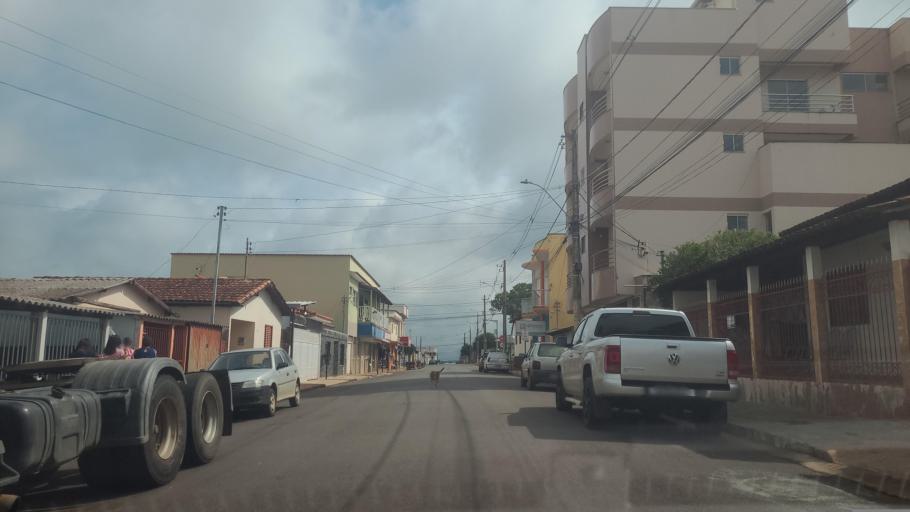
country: BR
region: Minas Gerais
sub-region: Carmo Do Paranaiba
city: Carmo do Paranaiba
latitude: -19.1951
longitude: -46.2426
